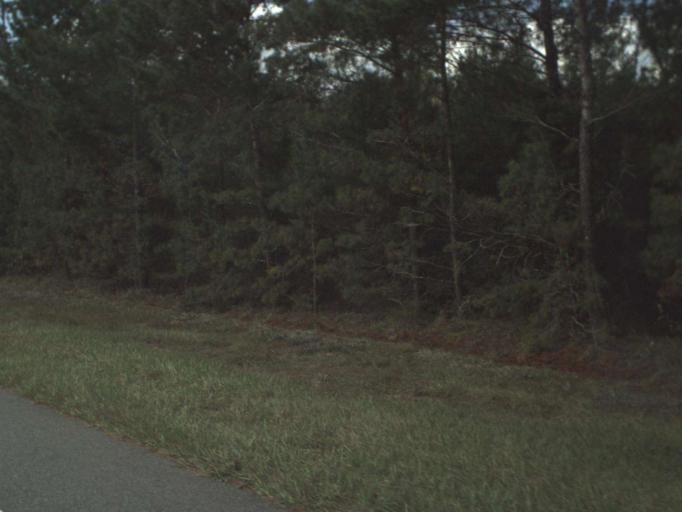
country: US
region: Florida
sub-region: Bay County
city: Youngstown
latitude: 30.4353
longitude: -85.3759
